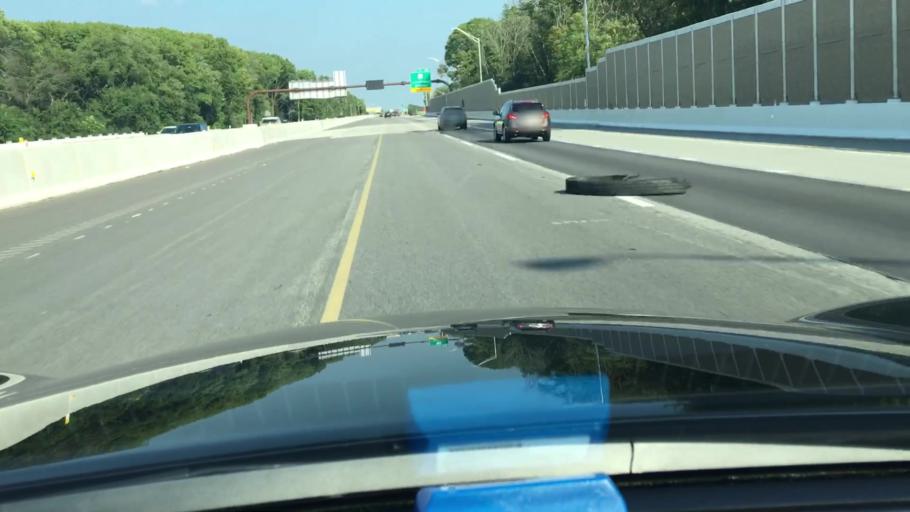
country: US
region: Pennsylvania
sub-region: Bucks County
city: Bristol
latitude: 40.1247
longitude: -74.8616
